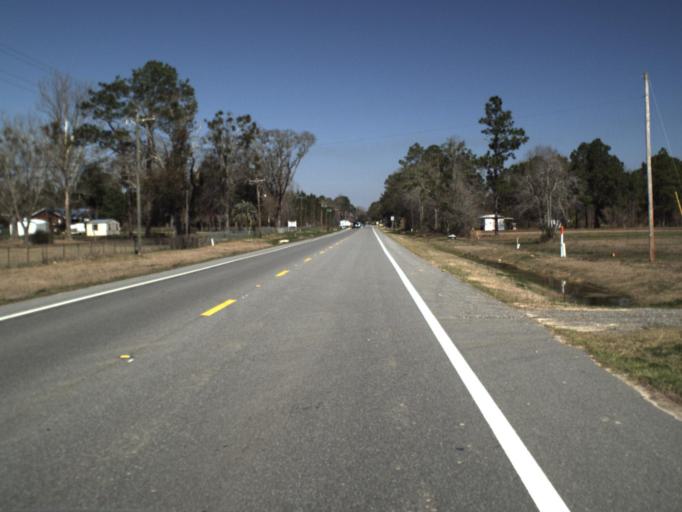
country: US
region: Florida
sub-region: Jackson County
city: Sneads
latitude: 30.6978
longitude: -85.0203
